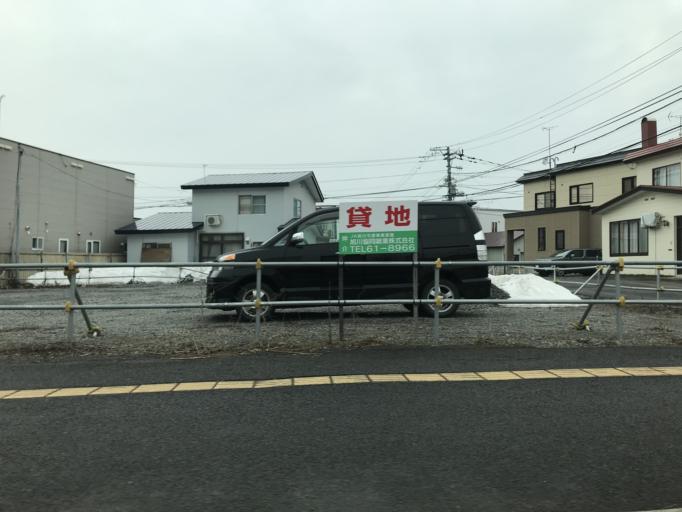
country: JP
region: Hokkaido
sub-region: Asahikawa-shi
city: Asahikawa
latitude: 43.7624
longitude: 142.3460
